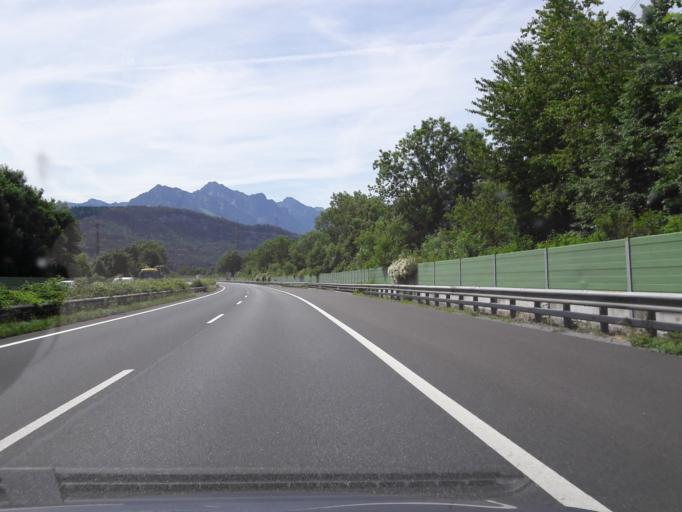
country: AT
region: Vorarlberg
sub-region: Politischer Bezirk Feldkirch
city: Rankweil
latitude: 47.2760
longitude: 9.6219
